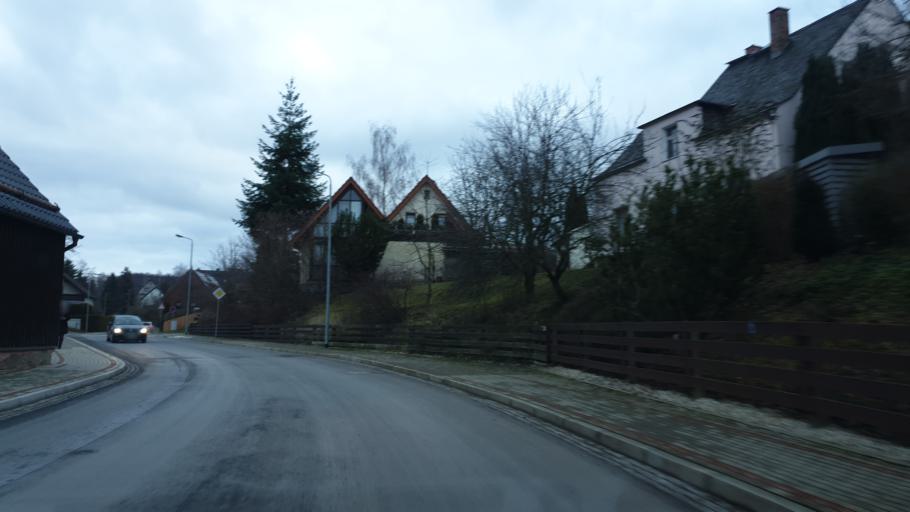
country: DE
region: Saxony
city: Lichtenstein
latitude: 50.7444
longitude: 12.6464
